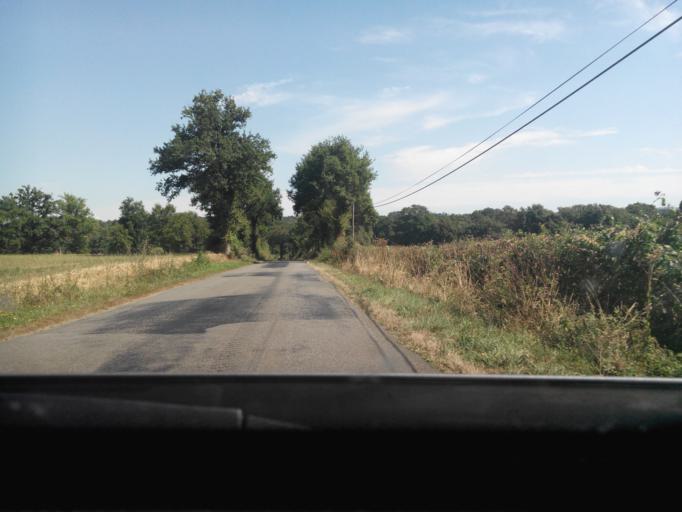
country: FR
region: Poitou-Charentes
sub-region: Departement de la Charente
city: Etagnac
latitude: 45.9388
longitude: 0.7718
